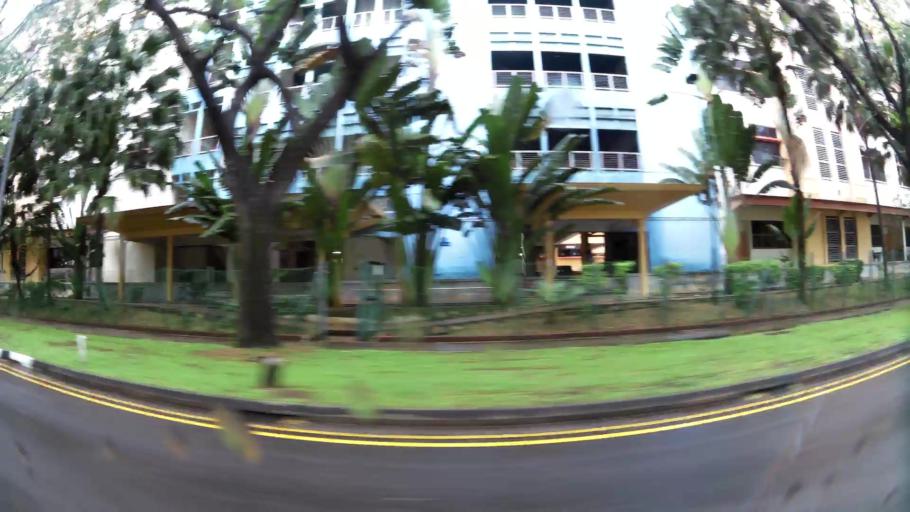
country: SG
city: Singapore
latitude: 1.3785
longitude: 103.8701
